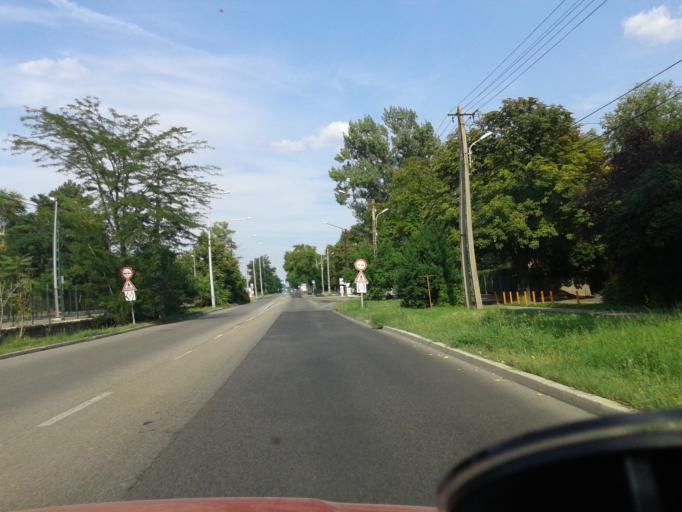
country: HU
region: Budapest
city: Budapest XVI. keruelet
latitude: 47.5132
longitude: 19.1990
